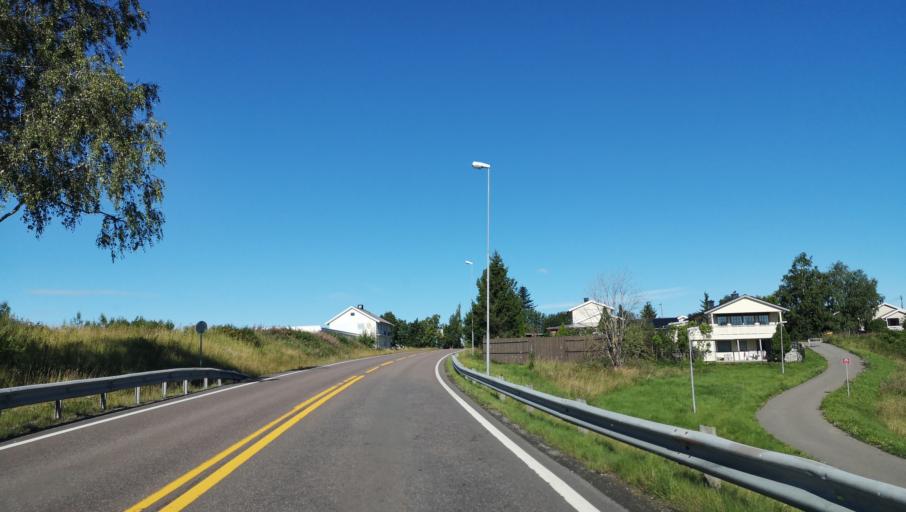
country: NO
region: Ostfold
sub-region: Spydeberg
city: Spydeberg
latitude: 59.6111
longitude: 11.0915
